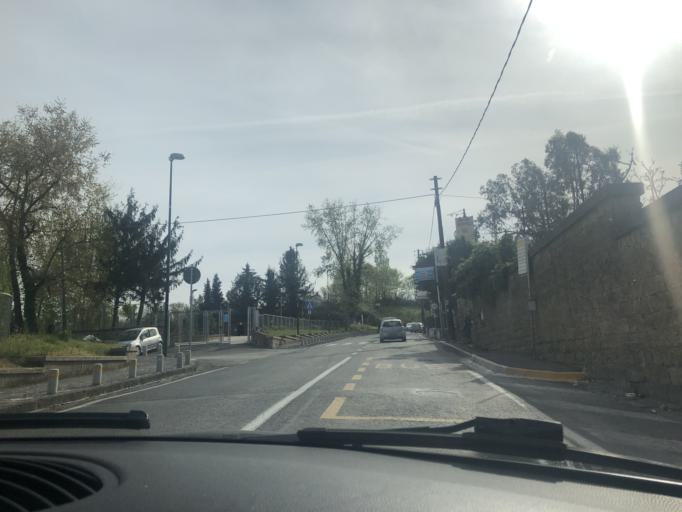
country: IT
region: Campania
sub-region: Provincia di Napoli
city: Torre Caracciolo
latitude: 40.8680
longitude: 14.2041
